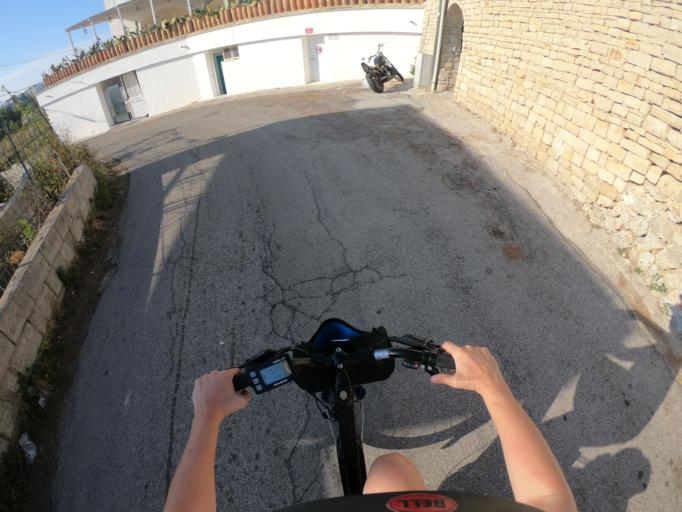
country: IT
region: Apulia
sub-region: Provincia di Lecce
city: Leuca
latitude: 39.7987
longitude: 18.3626
